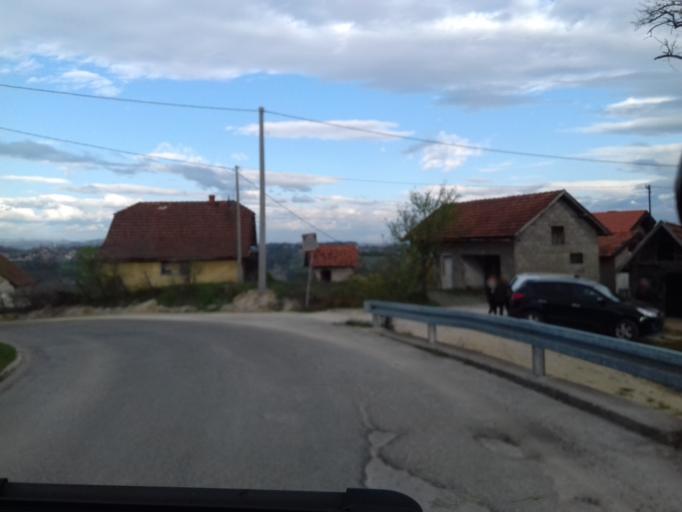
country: BA
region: Federation of Bosnia and Herzegovina
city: Tesanjka
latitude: 44.6482
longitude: 18.0296
